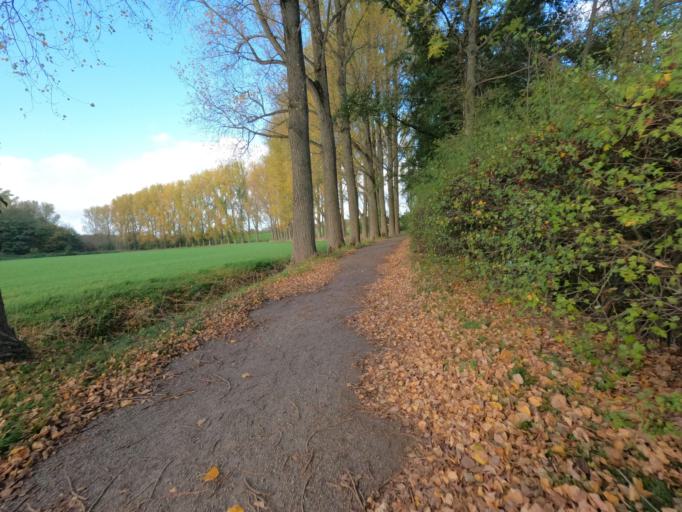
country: DE
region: North Rhine-Westphalia
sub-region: Regierungsbezirk Koln
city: Titz
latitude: 51.0850
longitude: 6.4115
